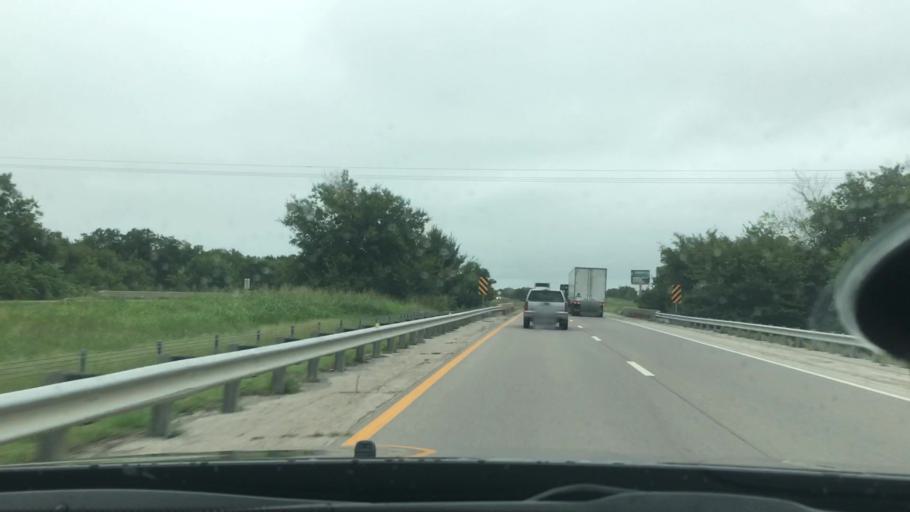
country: US
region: Oklahoma
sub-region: Okfuskee County
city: Okemah
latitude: 35.4283
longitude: -96.2478
